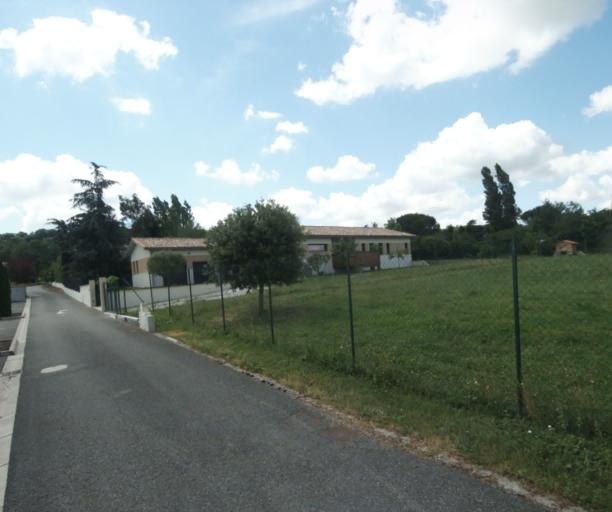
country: FR
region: Midi-Pyrenees
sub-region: Departement de la Haute-Garonne
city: Revel
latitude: 43.4493
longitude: 1.9948
